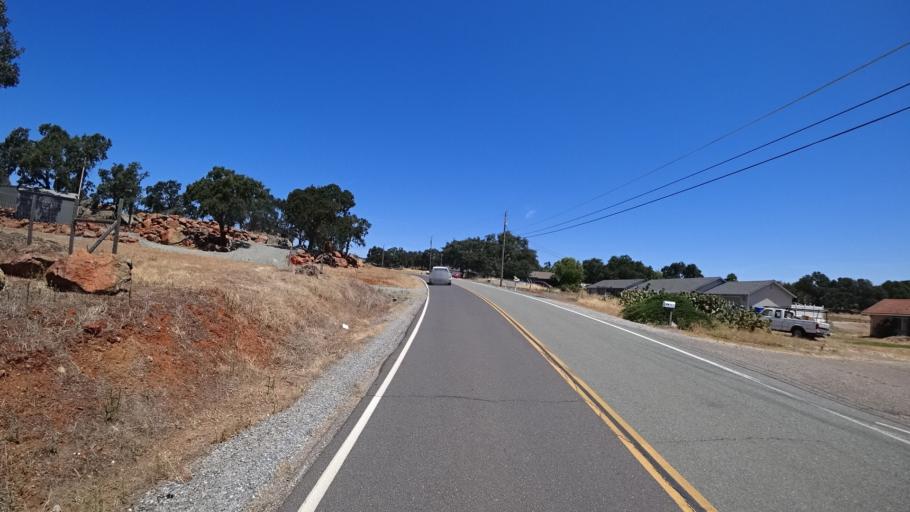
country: US
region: California
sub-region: Calaveras County
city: Rancho Calaveras
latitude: 38.1365
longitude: -120.8427
